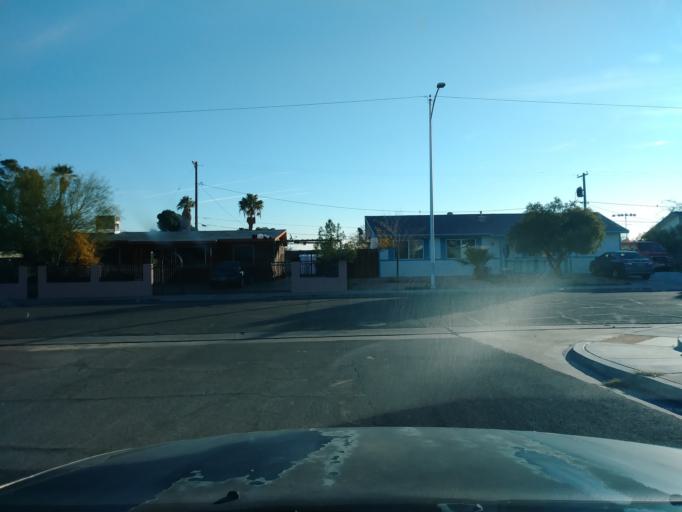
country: US
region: Nevada
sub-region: Clark County
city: Spring Valley
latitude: 36.1650
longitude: -115.2367
